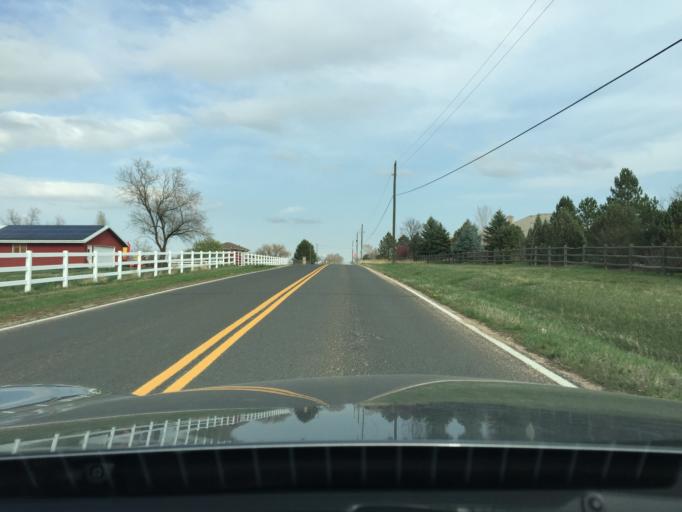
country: US
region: Colorado
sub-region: Boulder County
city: Niwot
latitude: 40.1162
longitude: -105.1282
